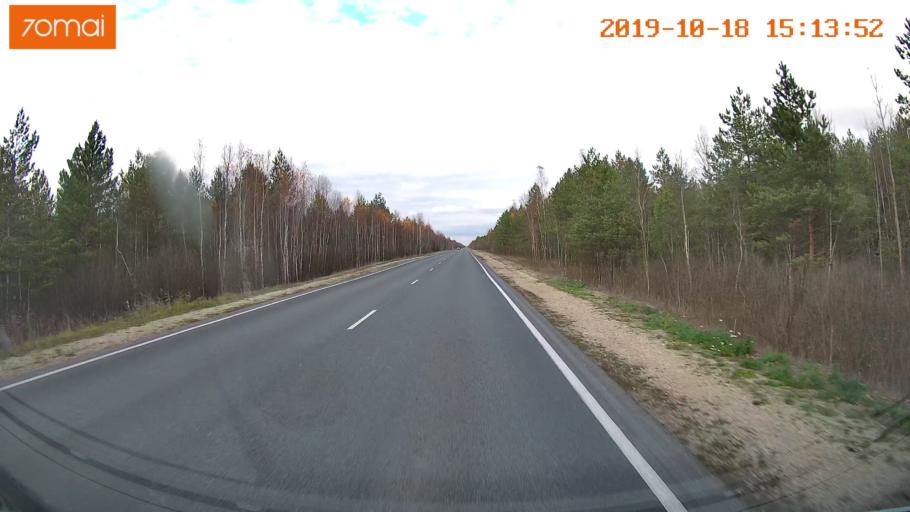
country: RU
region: Vladimir
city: Gus'-Khrustal'nyy
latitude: 55.5933
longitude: 40.7191
